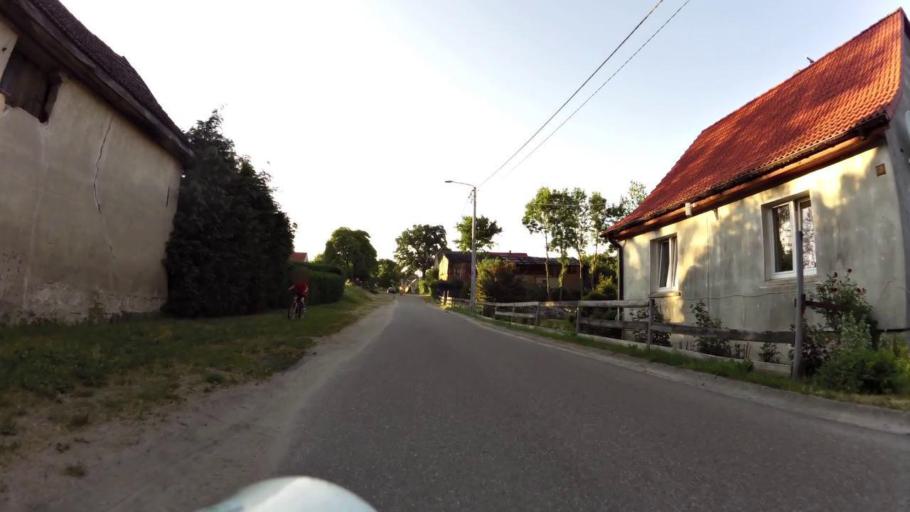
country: PL
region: West Pomeranian Voivodeship
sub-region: Powiat szczecinecki
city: Szczecinek
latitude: 53.8021
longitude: 16.6883
